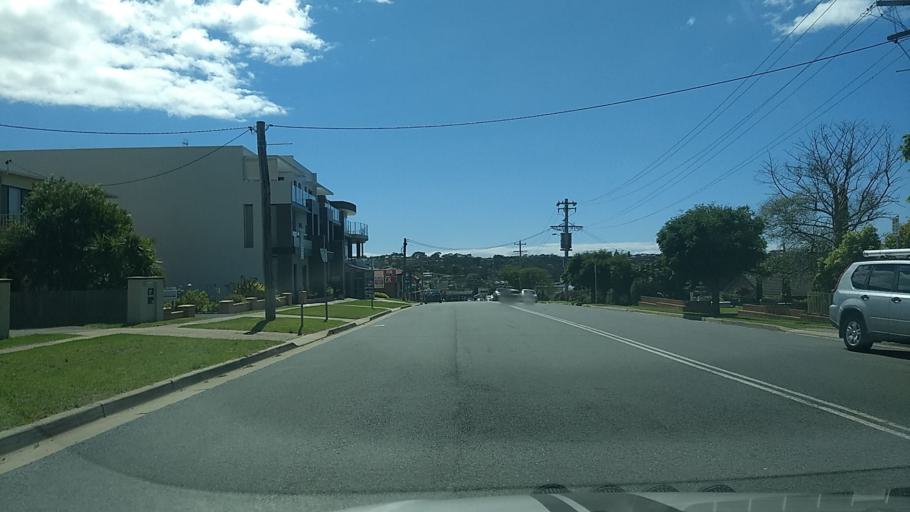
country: AU
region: New South Wales
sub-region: Bega Valley
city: Merimbula
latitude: -36.8879
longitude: 149.9074
